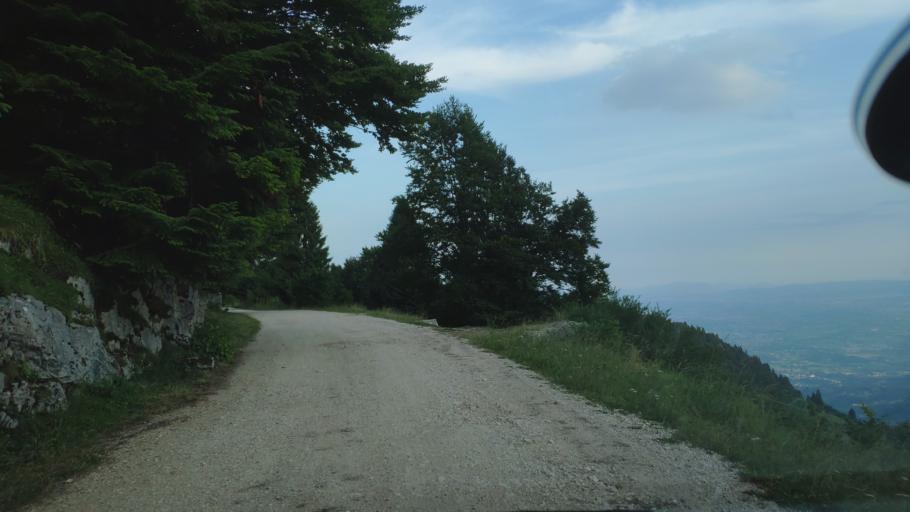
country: IT
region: Veneto
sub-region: Provincia di Vicenza
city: Calvene
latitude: 45.8017
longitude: 11.5041
